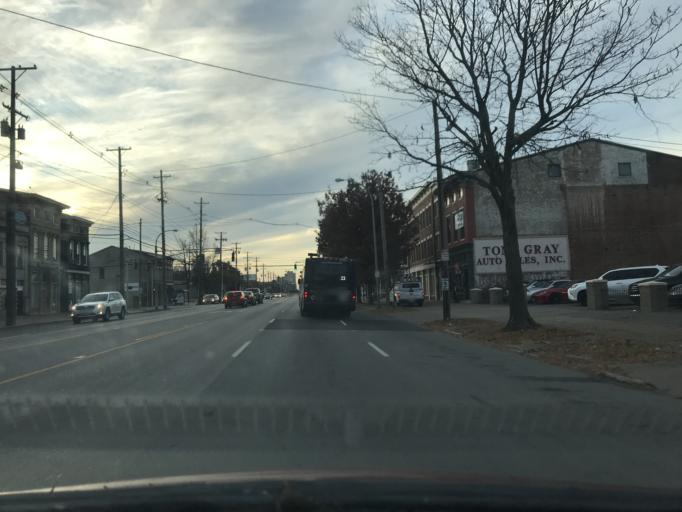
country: US
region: Kentucky
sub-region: Jefferson County
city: Louisville
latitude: 38.2447
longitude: -85.7386
